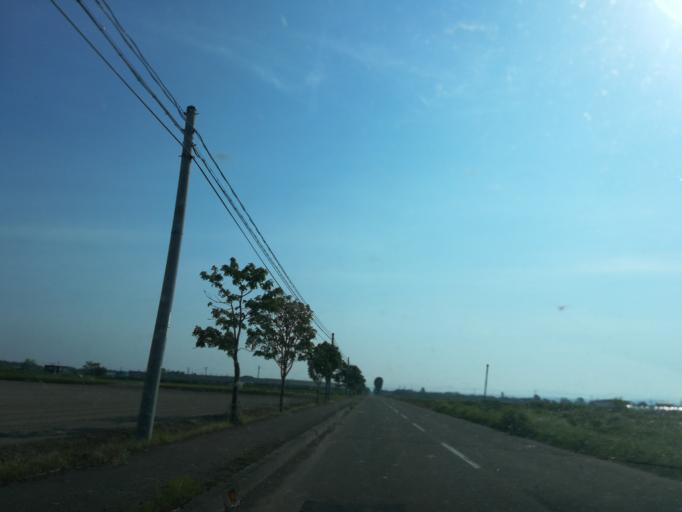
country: JP
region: Hokkaido
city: Iwamizawa
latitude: 43.1654
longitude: 141.6953
